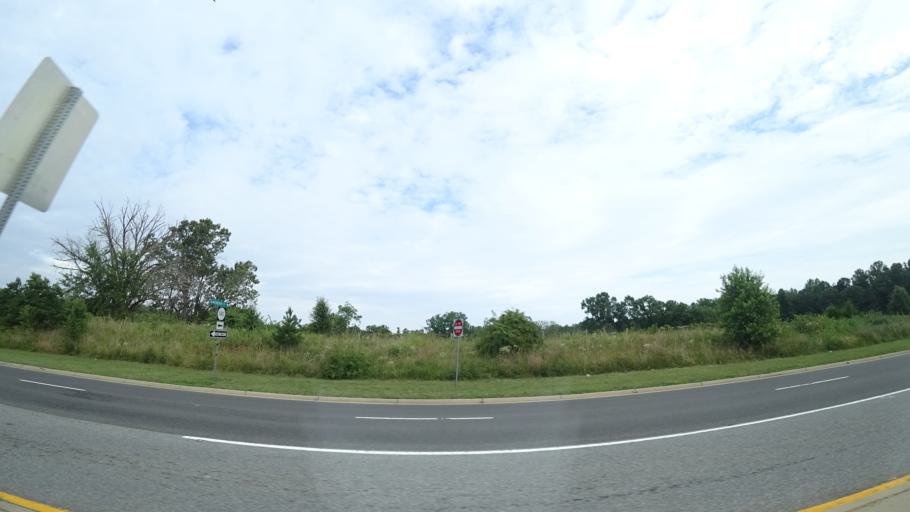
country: US
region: Virginia
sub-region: Spotsylvania County
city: Spotsylvania
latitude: 38.2090
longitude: -77.5785
